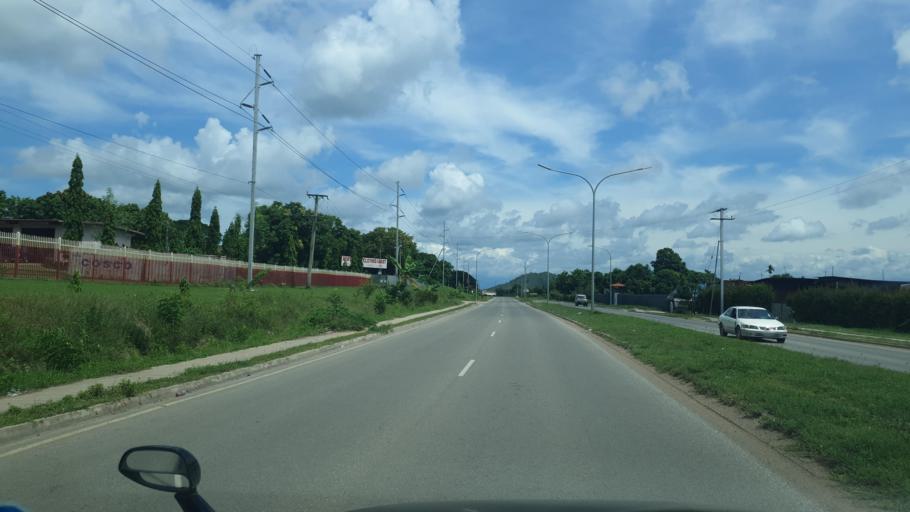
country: PG
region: National Capital
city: Port Moresby
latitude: -9.3857
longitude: 147.1549
